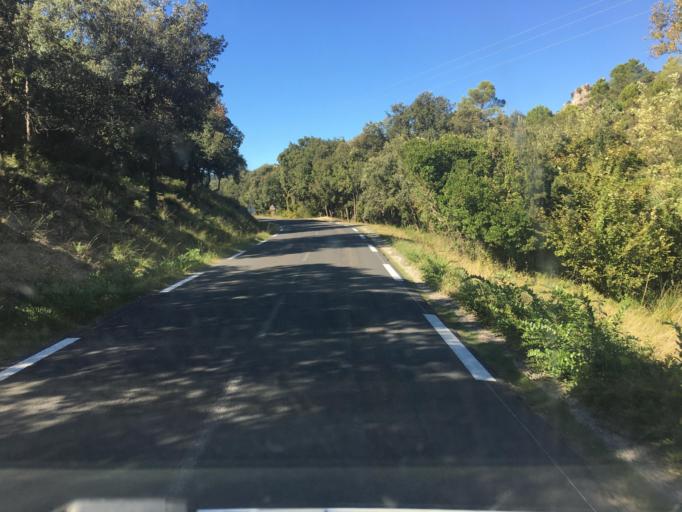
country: FR
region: Languedoc-Roussillon
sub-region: Departement de l'Herault
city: Nebian
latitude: 43.6168
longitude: 3.3661
